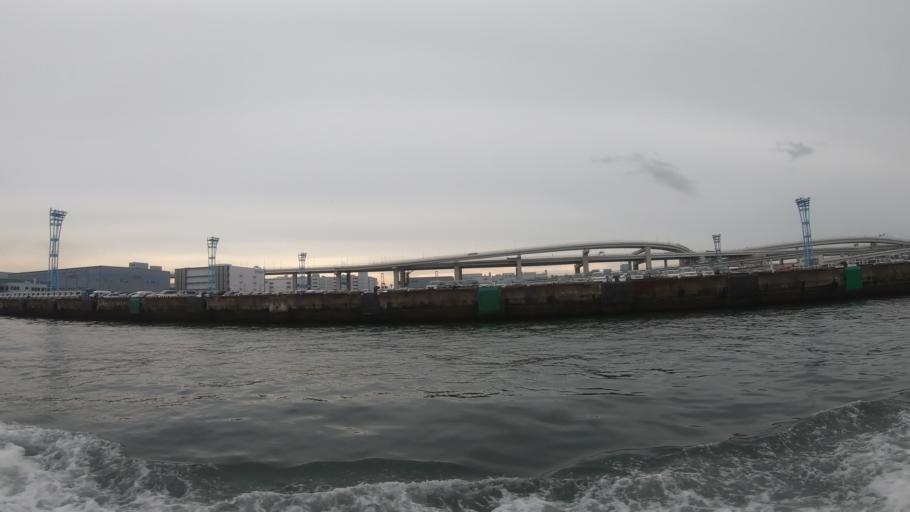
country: JP
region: Kanagawa
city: Yokohama
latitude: 35.4692
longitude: 139.6820
